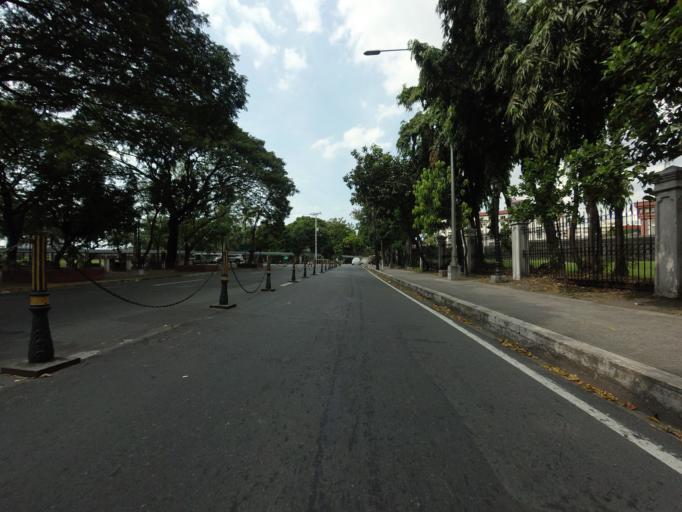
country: PH
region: Metro Manila
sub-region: City of Manila
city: Port Area
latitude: 14.5856
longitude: 120.9789
